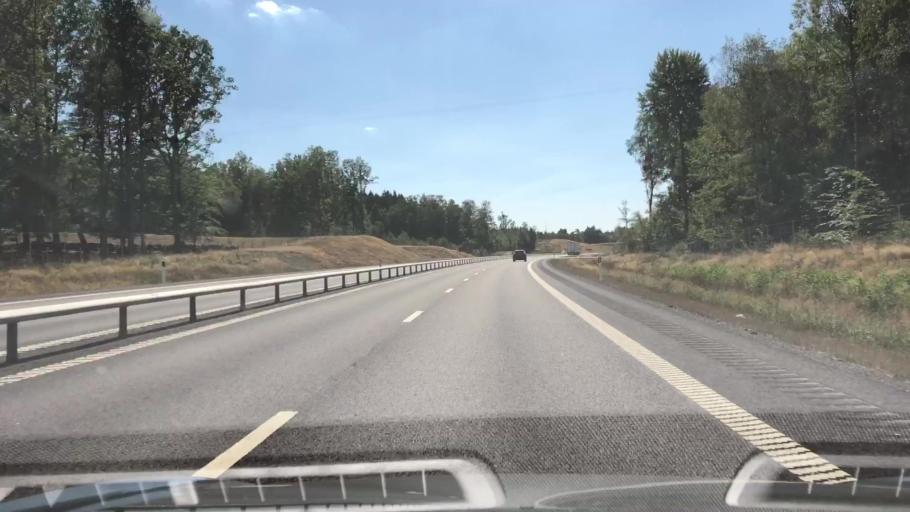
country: SE
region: Skane
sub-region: Hassleholms Kommun
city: Vinslov
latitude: 55.9311
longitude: 13.8441
